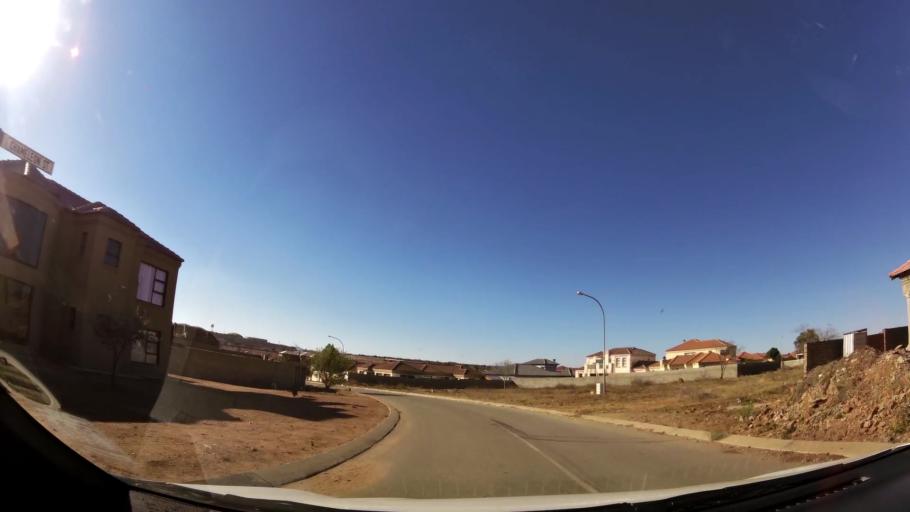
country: ZA
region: Limpopo
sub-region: Capricorn District Municipality
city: Polokwane
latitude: -23.9071
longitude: 29.5055
